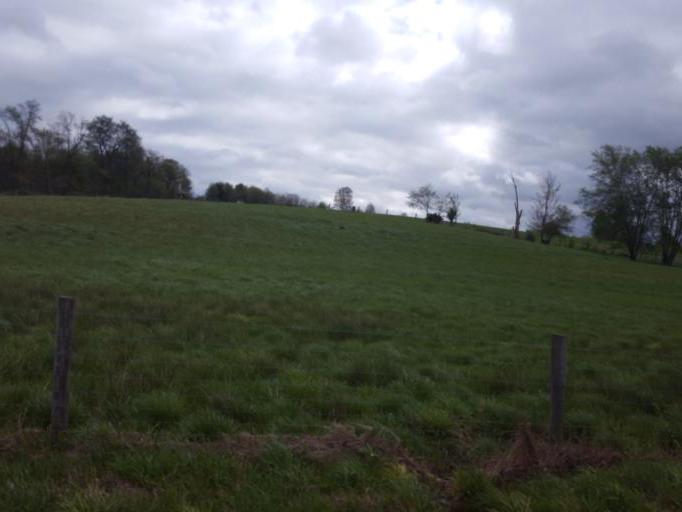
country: US
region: Ohio
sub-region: Sandusky County
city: Bellville
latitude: 40.5502
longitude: -82.5090
